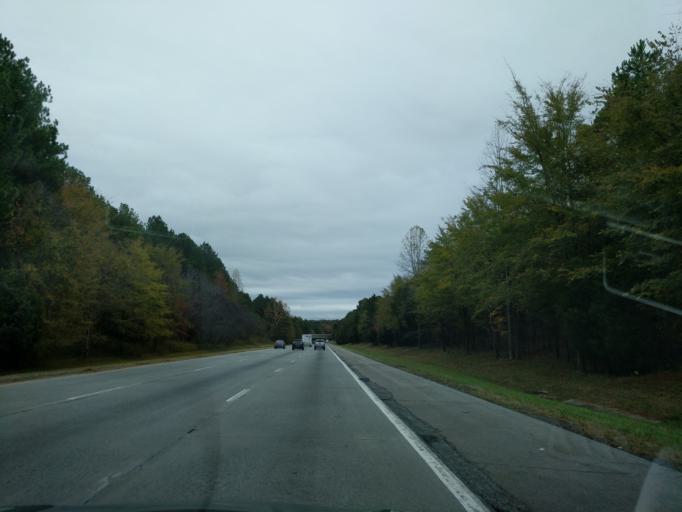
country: US
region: North Carolina
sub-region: Davidson County
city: Lexington
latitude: 35.8243
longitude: -80.1665
